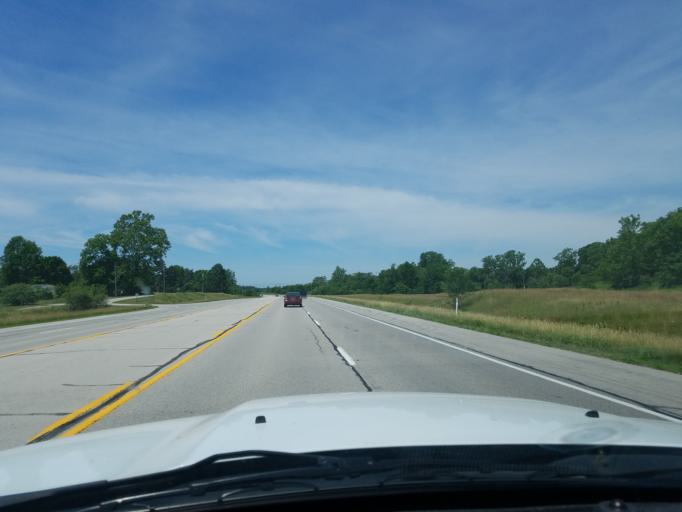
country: US
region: Indiana
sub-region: Delaware County
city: Yorktown
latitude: 40.1208
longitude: -85.4669
